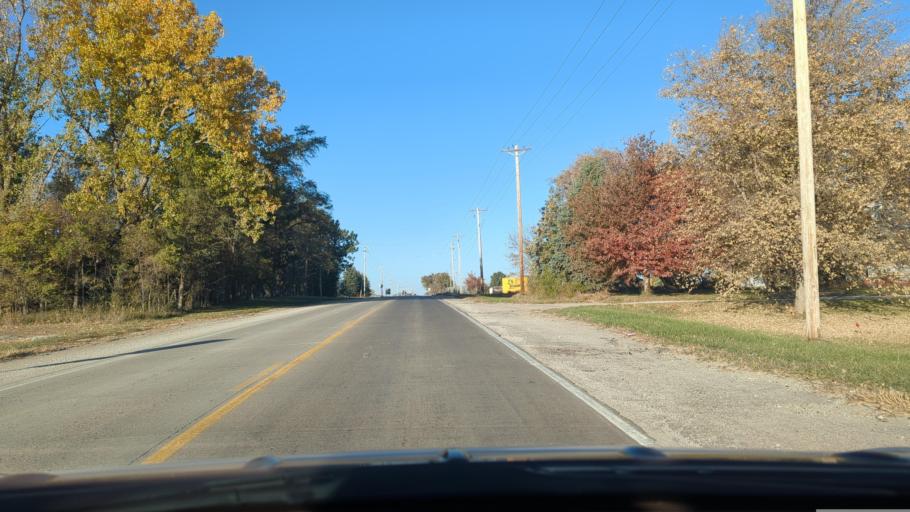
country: US
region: Nebraska
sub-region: Sarpy County
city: Springfield
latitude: 41.1036
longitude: -96.1561
